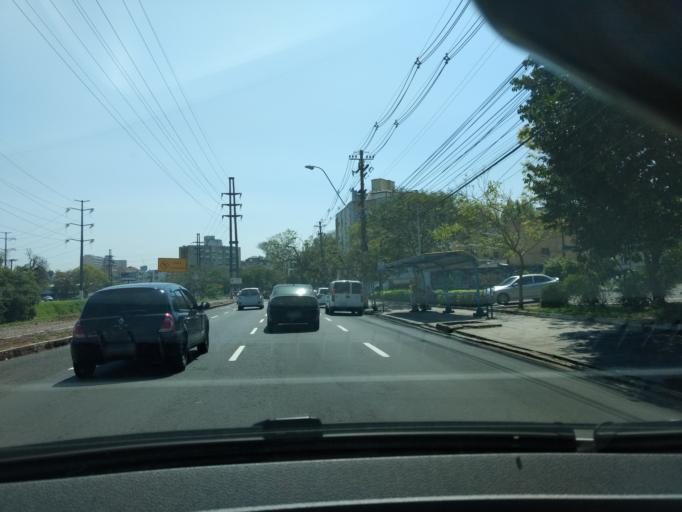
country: BR
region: Rio Grande do Sul
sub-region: Porto Alegre
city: Porto Alegre
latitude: -30.0449
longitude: -51.1987
